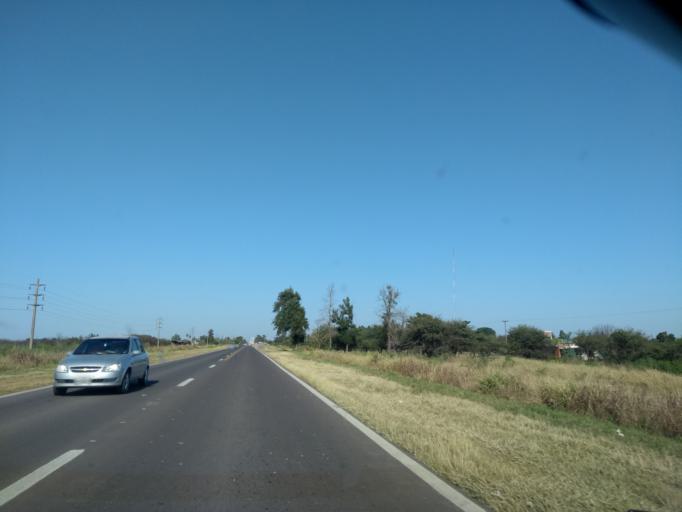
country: AR
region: Chaco
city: Presidencia Roque Saenz Pena
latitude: -26.7719
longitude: -60.4006
